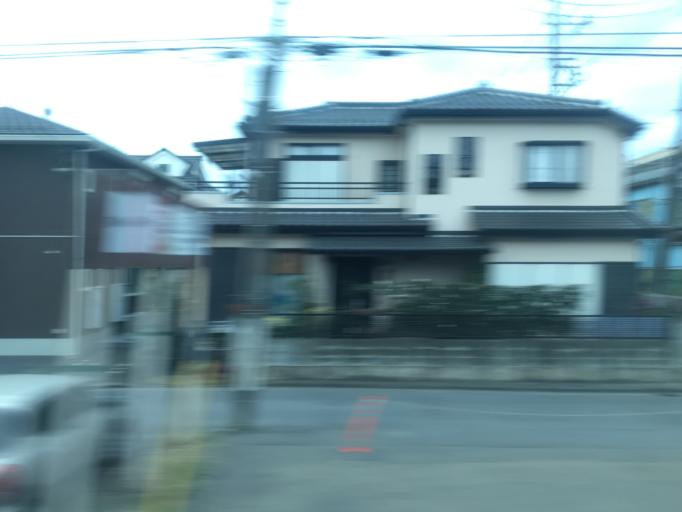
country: JP
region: Saitama
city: Ageoshimo
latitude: 35.9687
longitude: 139.5924
